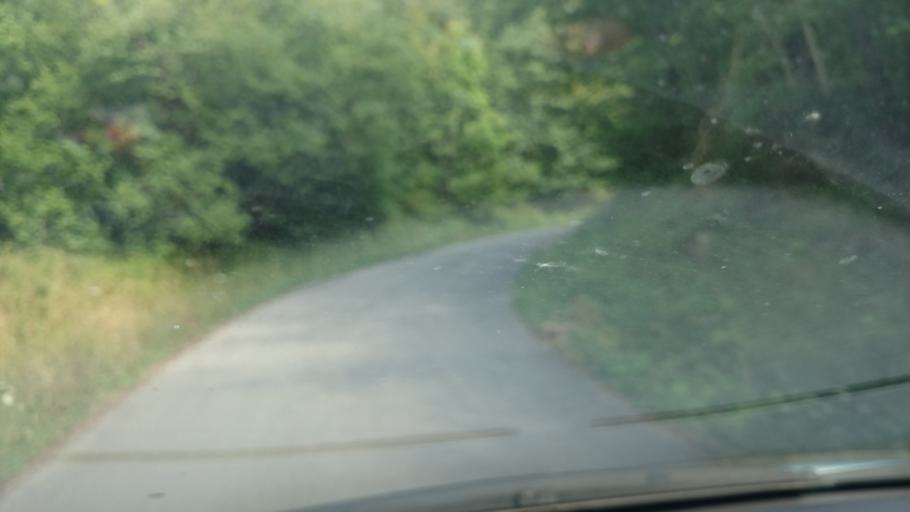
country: IT
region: Emilia-Romagna
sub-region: Provincia di Reggio Emilia
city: Villa Minozzo
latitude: 44.3094
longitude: 10.4561
